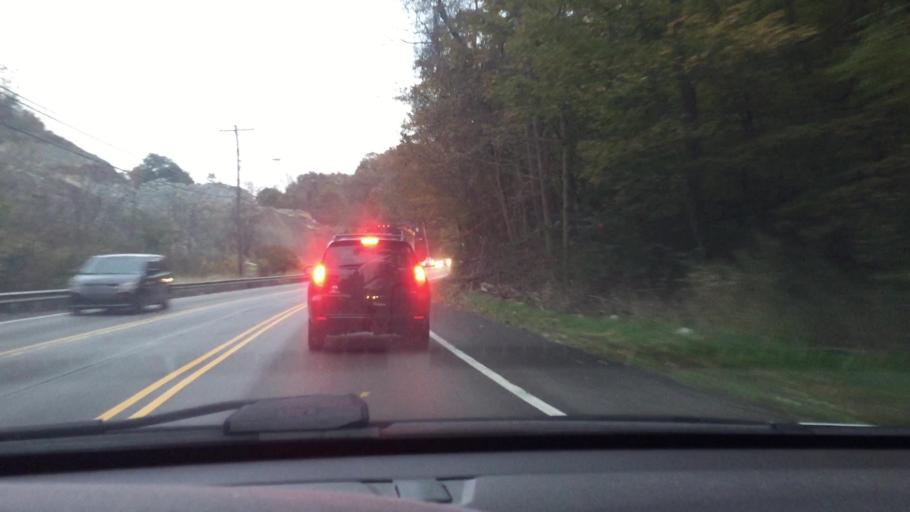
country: US
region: Pennsylvania
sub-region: Allegheny County
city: Ingram
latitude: 40.4462
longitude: -80.1006
